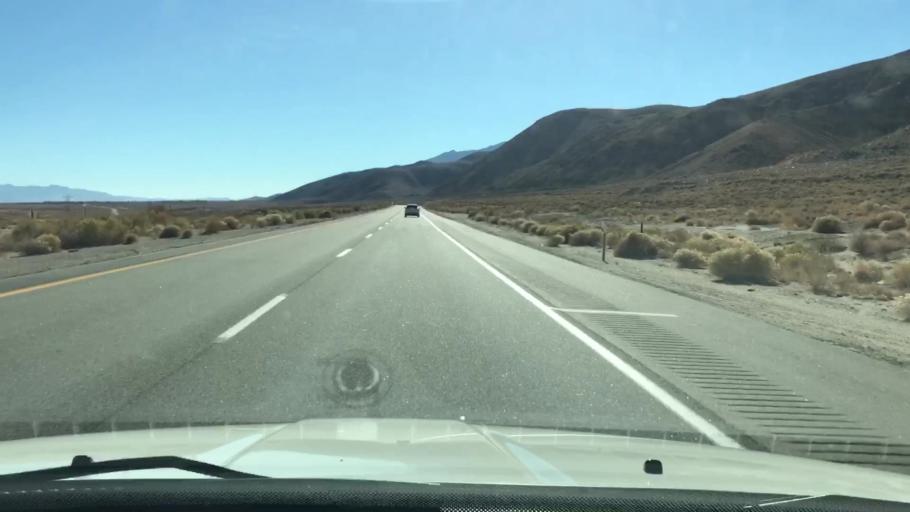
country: US
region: California
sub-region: Inyo County
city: Lone Pine
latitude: 36.6675
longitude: -118.0954
